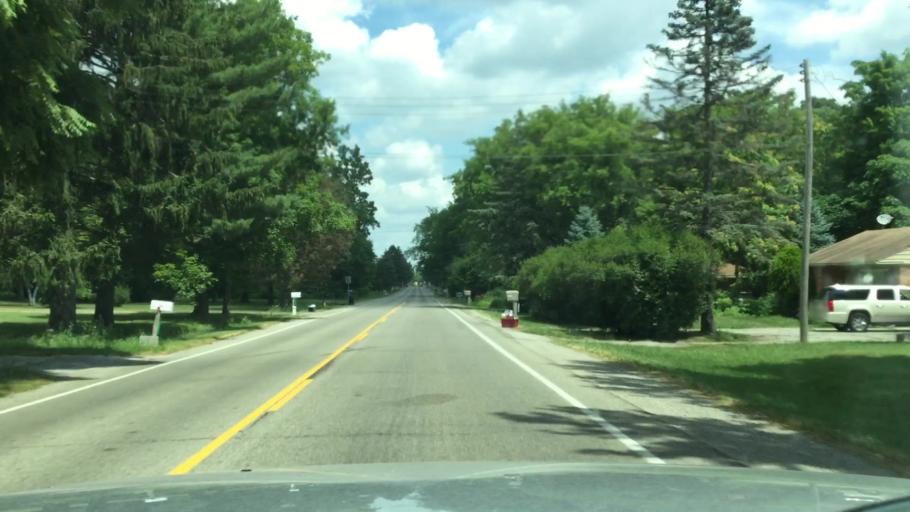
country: US
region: Michigan
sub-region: Genesee County
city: Flushing
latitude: 43.0755
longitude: -83.8721
